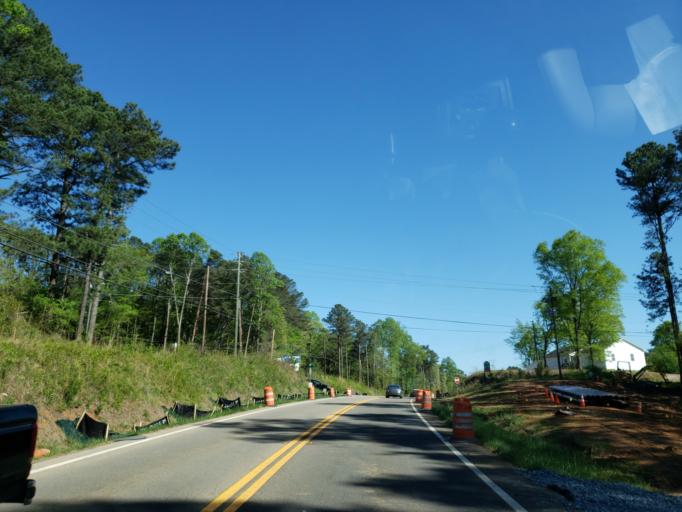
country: US
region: Georgia
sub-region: Cherokee County
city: Canton
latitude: 34.2829
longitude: -84.5116
